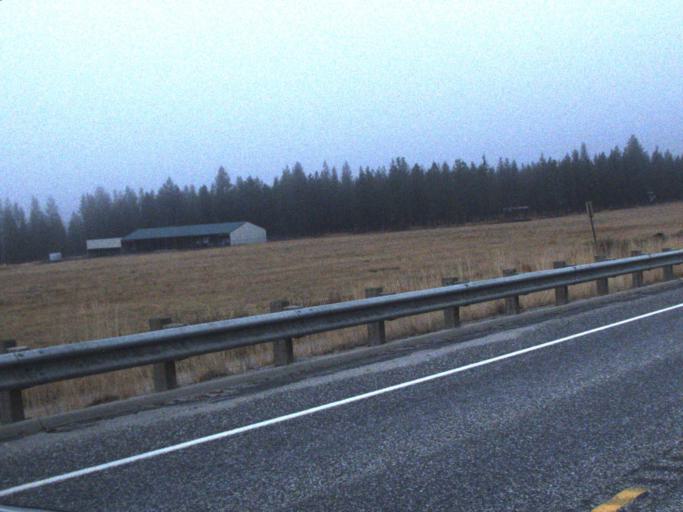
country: US
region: Washington
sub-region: Stevens County
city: Kettle Falls
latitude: 48.6917
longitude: -118.1250
